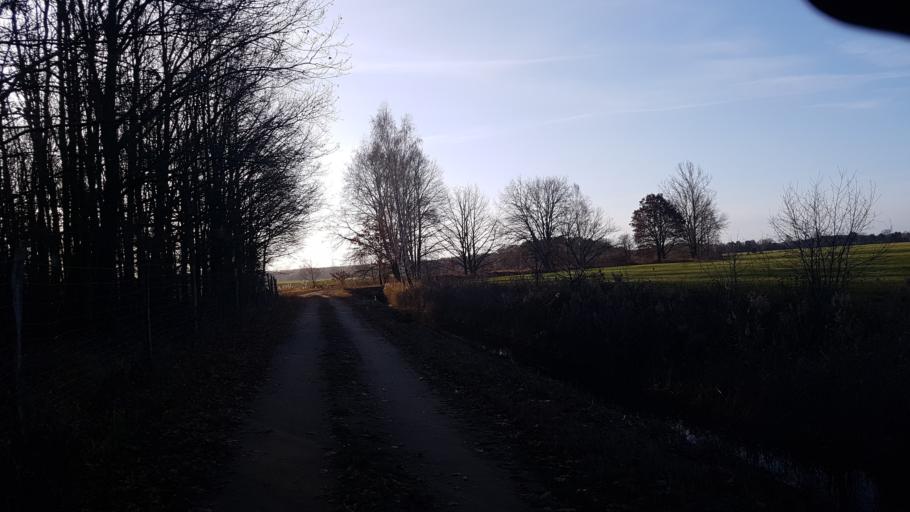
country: DE
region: Brandenburg
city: Schonborn
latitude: 51.5717
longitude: 13.4951
